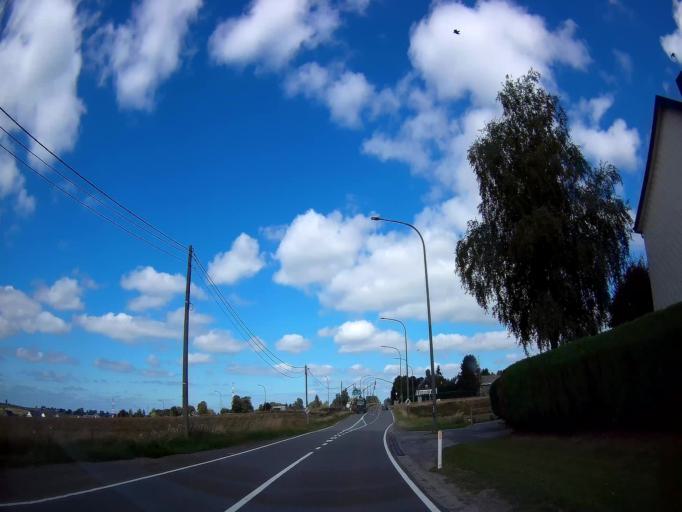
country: BE
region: Wallonia
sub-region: Province du Luxembourg
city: Bastogne
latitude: 50.0145
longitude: 5.7094
